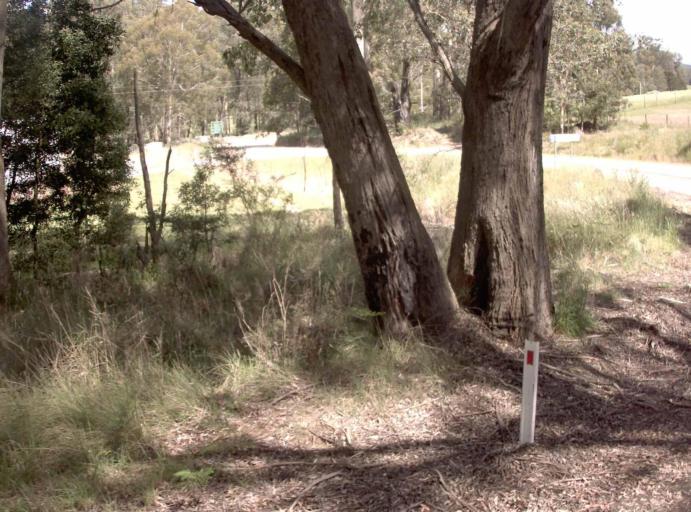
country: AU
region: New South Wales
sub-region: Bombala
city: Bombala
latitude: -37.1875
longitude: 148.7255
